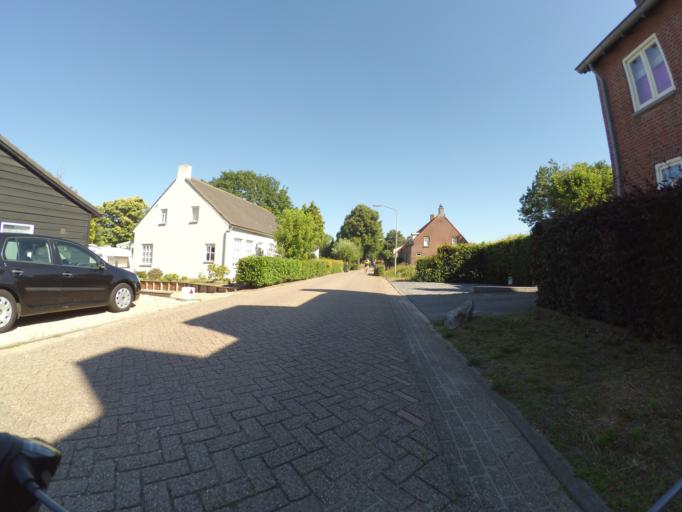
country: NL
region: North Brabant
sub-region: Gemeente Made en Drimmelen
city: Made
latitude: 51.6719
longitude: 4.7770
